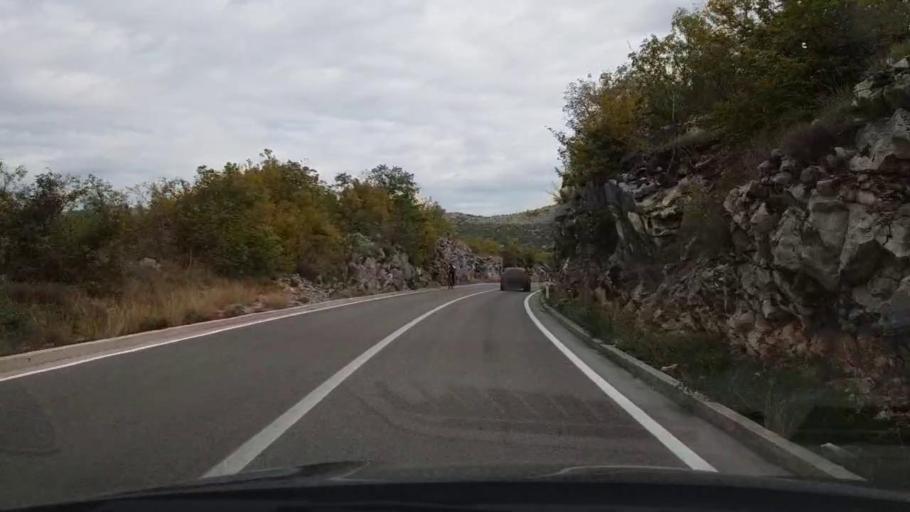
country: BA
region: Republika Srpska
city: Trebinje
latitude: 42.6832
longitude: 18.2950
